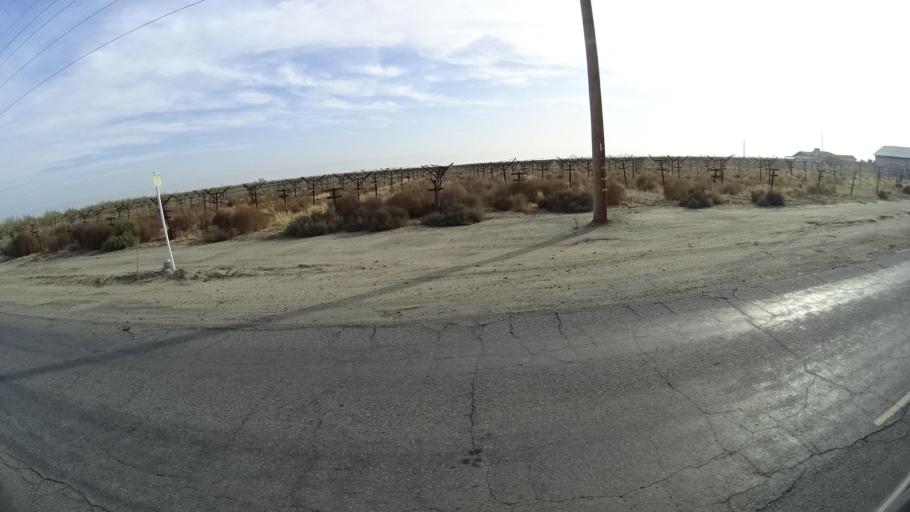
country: US
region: California
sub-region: Kern County
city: Delano
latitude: 35.7538
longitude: -119.2053
